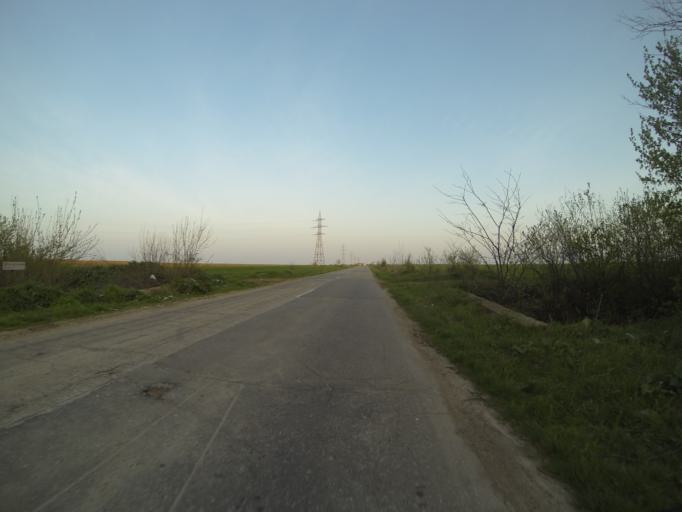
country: RO
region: Dolj
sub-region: Comuna Dranicu
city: Dranic
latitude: 44.0635
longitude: 23.8159
